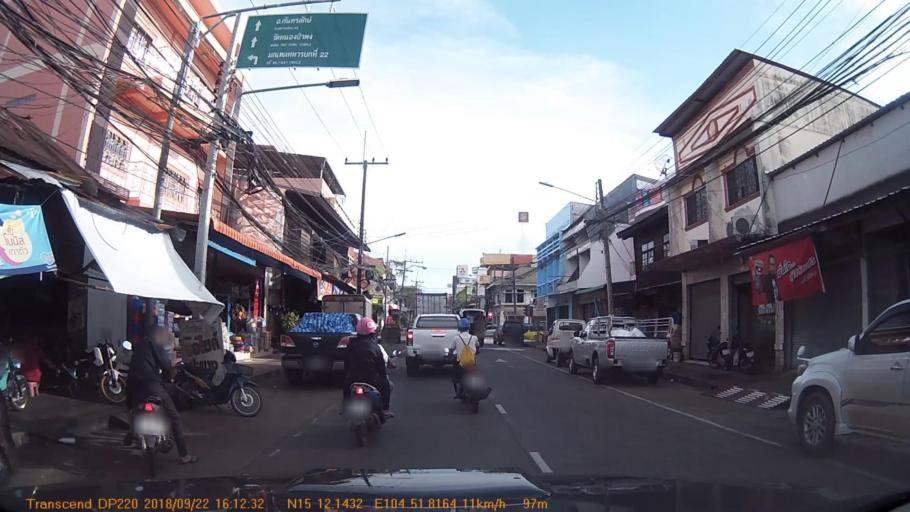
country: TH
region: Changwat Ubon Ratchathani
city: Warin Chamrap
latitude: 15.2024
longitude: 104.8636
